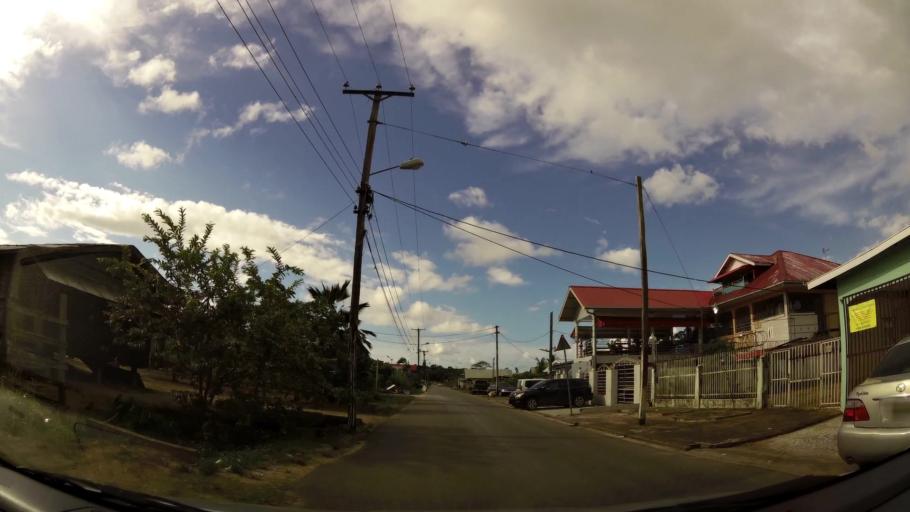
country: SR
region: Paramaribo
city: Paramaribo
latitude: 5.8548
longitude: -55.1782
